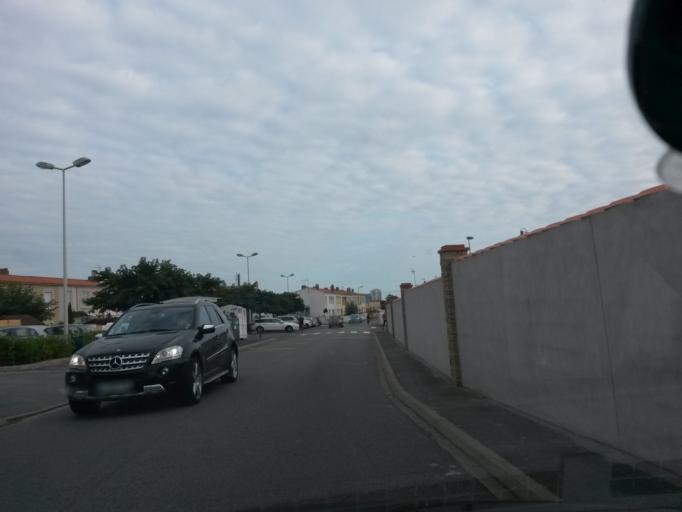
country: FR
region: Pays de la Loire
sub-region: Departement de la Vendee
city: Les Sables-d'Olonne
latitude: 46.4998
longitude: -1.8033
